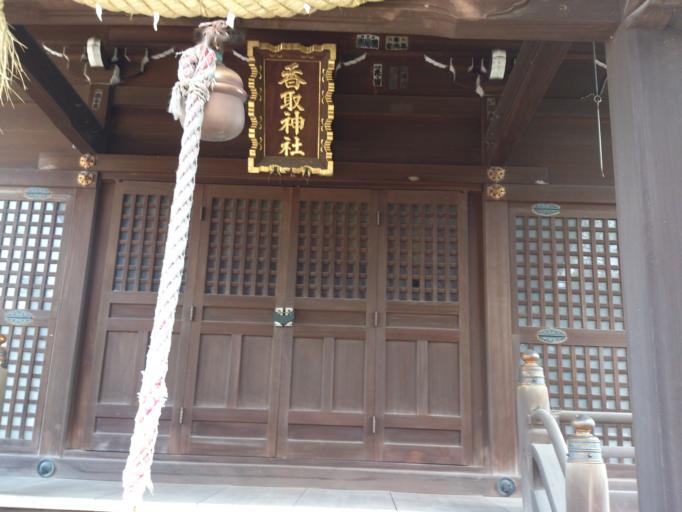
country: JP
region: Chiba
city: Kashiwa
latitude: 35.8382
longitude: 139.9469
